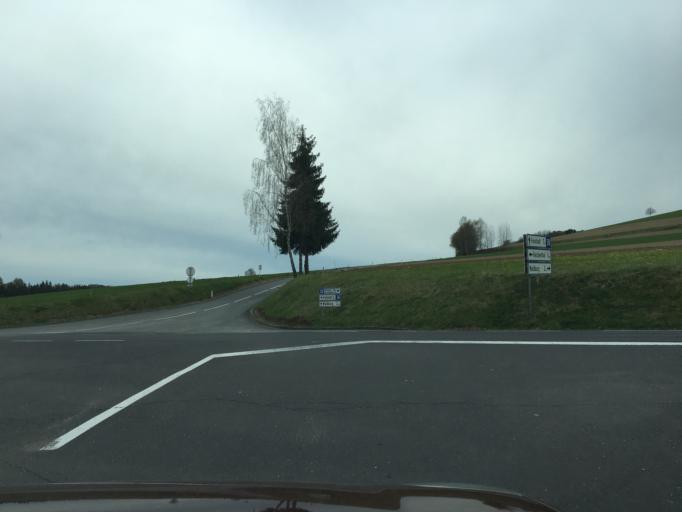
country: AT
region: Upper Austria
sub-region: Politischer Bezirk Urfahr-Umgebung
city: Reichenthal
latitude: 48.5197
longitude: 14.4291
